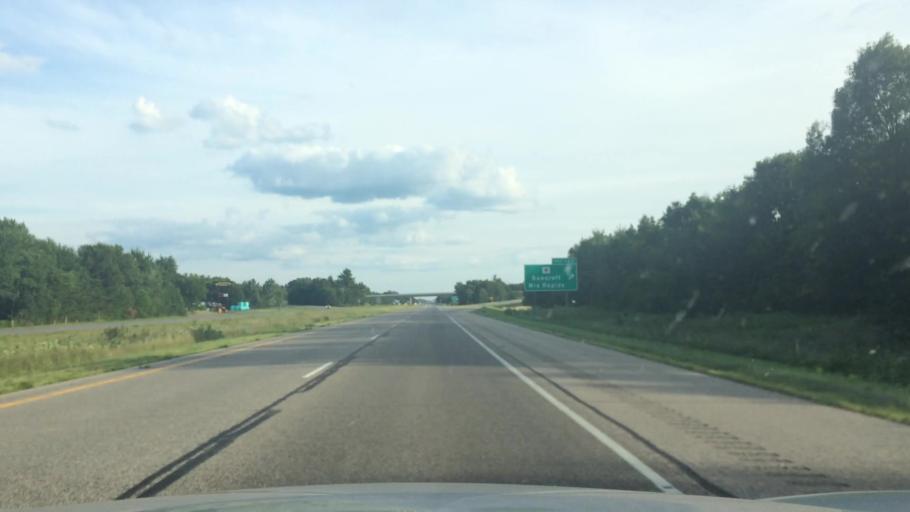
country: US
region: Wisconsin
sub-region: Portage County
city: Plover
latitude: 44.3149
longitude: -89.5236
